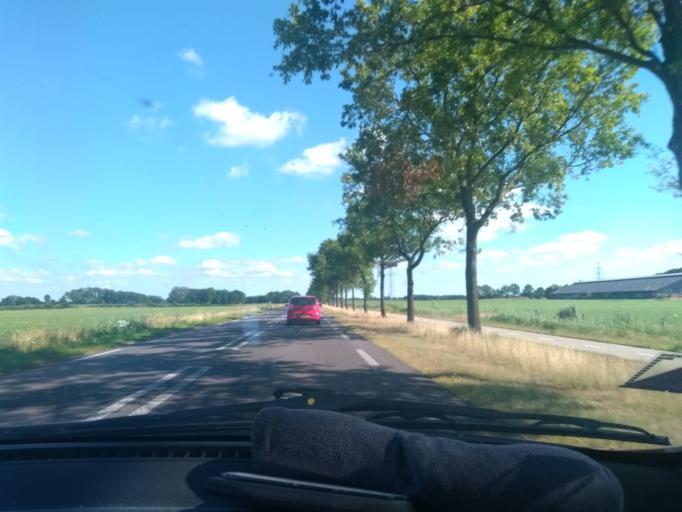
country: NL
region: Drenthe
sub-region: Gemeente Tynaarlo
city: Vries
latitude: 53.1209
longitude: 6.5067
